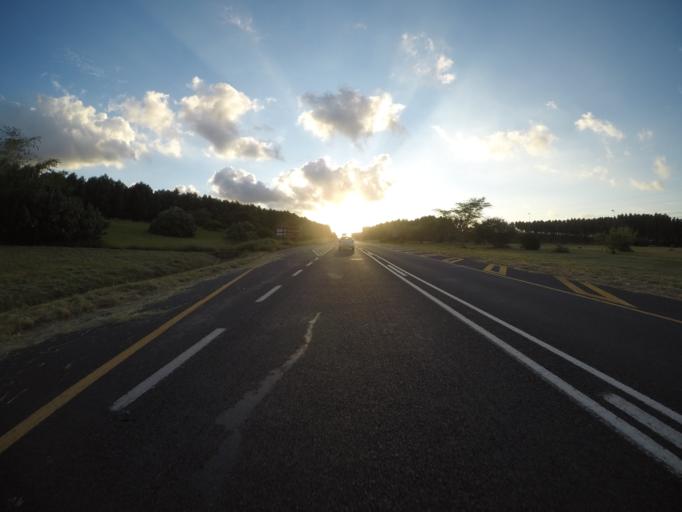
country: ZA
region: KwaZulu-Natal
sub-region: uThungulu District Municipality
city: Richards Bay
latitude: -28.6941
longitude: 32.0286
